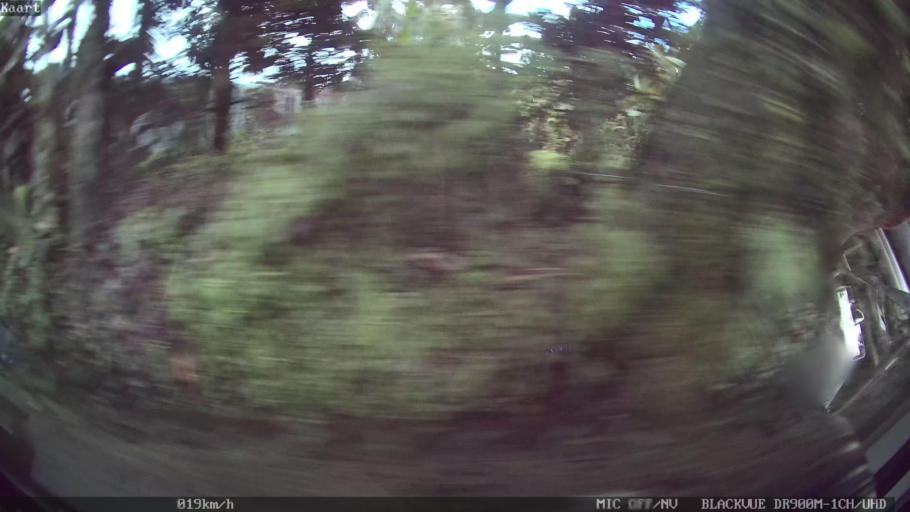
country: ID
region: Bali
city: Banjar Bucu
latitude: -8.5734
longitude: 115.2037
